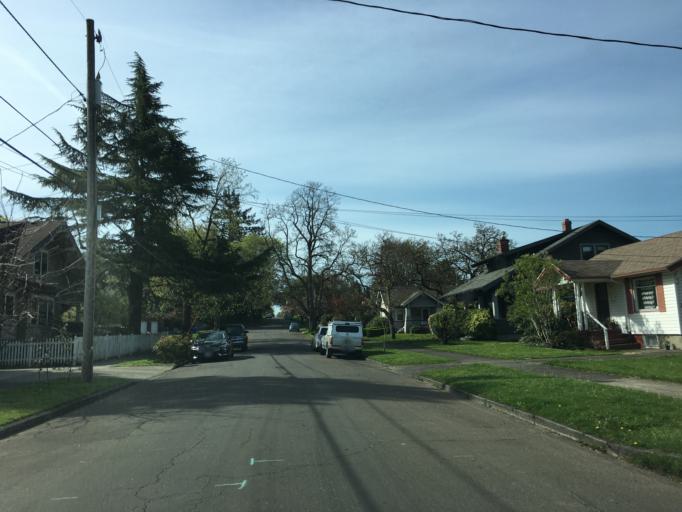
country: US
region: Oregon
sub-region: Multnomah County
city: Lents
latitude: 45.5252
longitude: -122.5771
